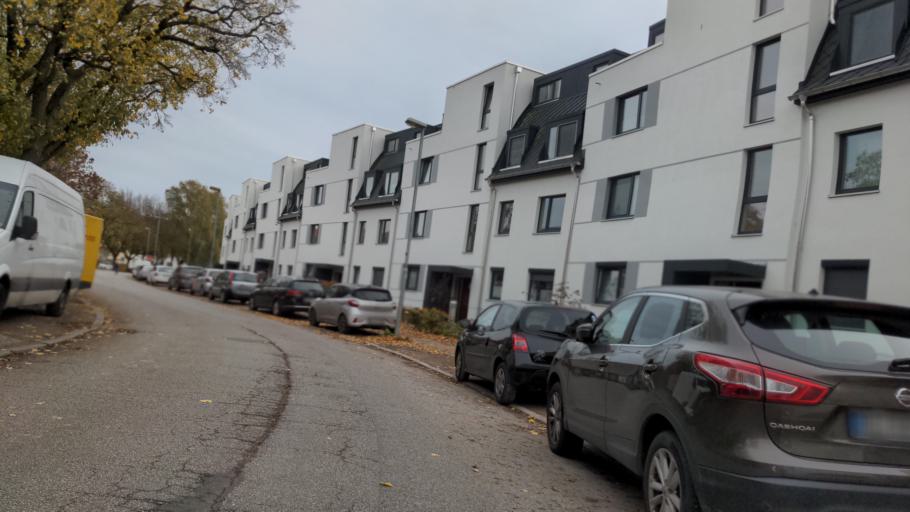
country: DE
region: Schleswig-Holstein
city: Luebeck
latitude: 53.8594
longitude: 10.6580
